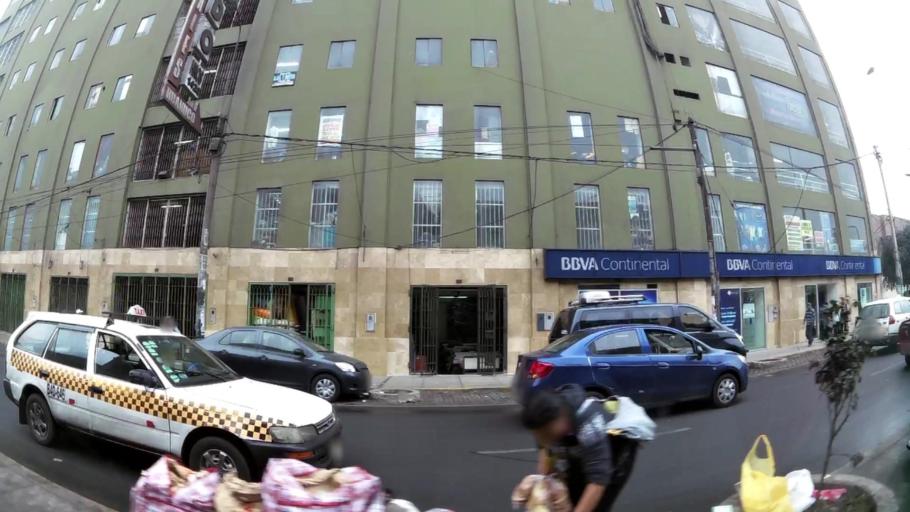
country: PE
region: Lima
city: Lima
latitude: -12.0617
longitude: -77.0153
